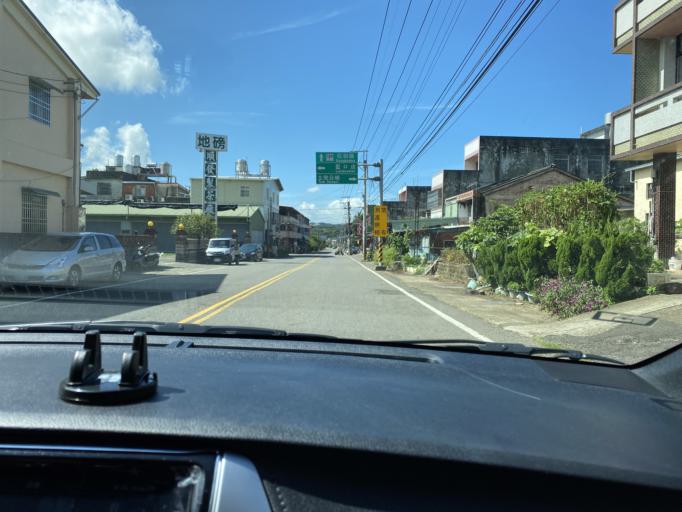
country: TW
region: Taiwan
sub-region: Nantou
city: Nantou
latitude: 23.8742
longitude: 120.6333
